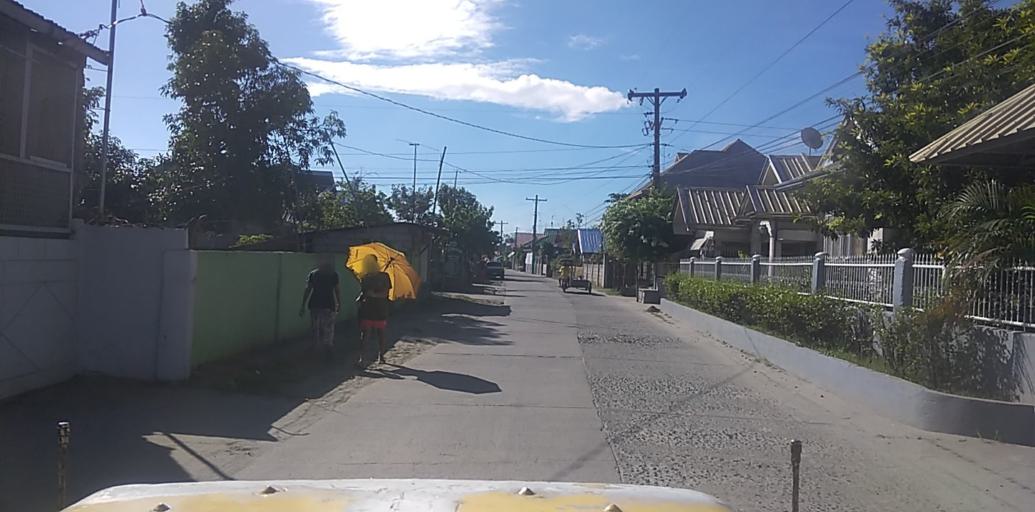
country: PH
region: Central Luzon
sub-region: Province of Pampanga
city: San Patricio
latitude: 15.1064
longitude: 120.7131
